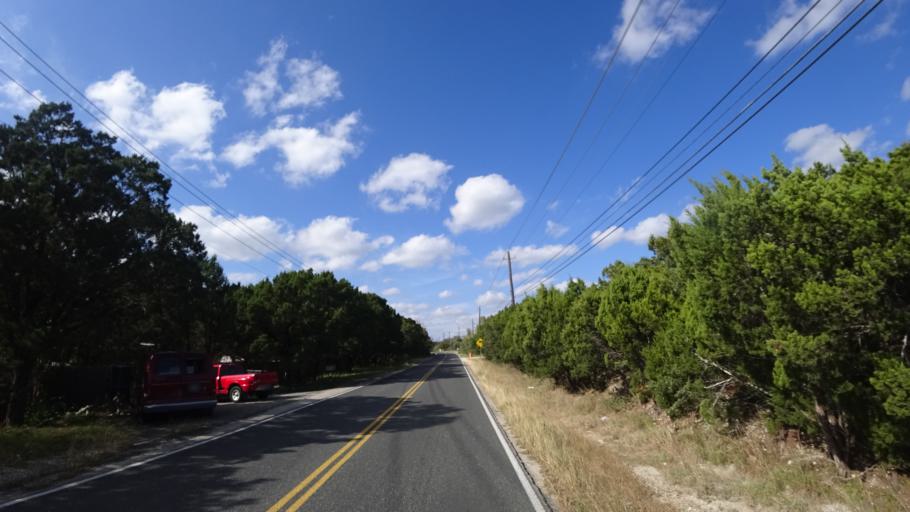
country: US
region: Texas
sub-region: Travis County
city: Barton Creek
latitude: 30.2430
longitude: -97.8789
